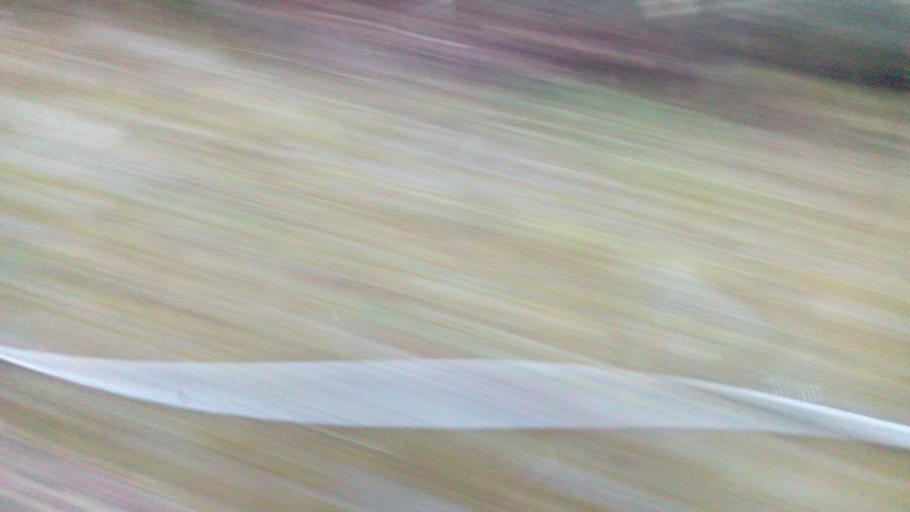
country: TW
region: Taiwan
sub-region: Hualien
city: Hualian
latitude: 24.3412
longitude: 121.3140
